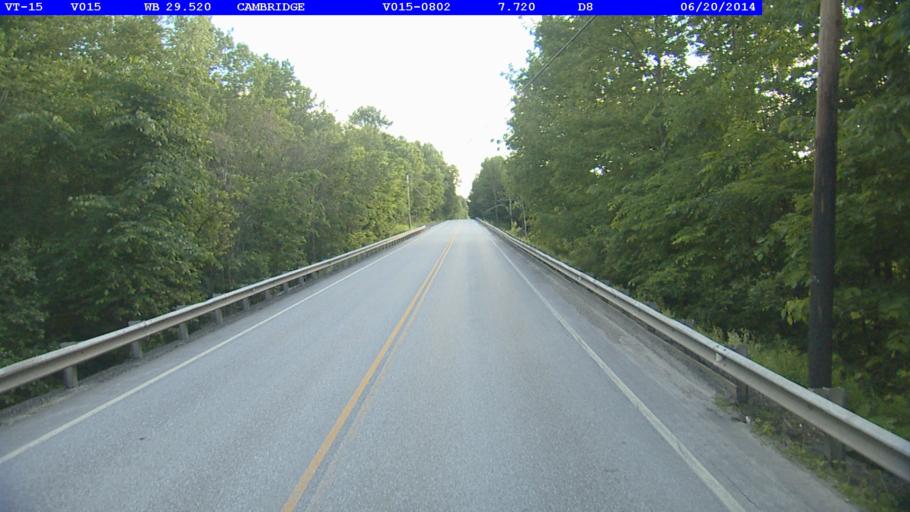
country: US
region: Vermont
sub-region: Lamoille County
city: Johnson
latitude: 44.6652
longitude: -72.7861
